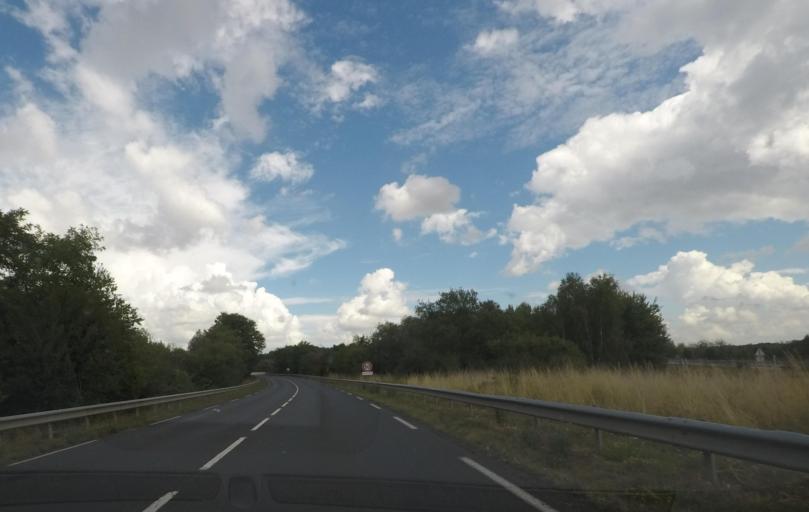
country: FR
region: Pays de la Loire
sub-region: Departement de la Sarthe
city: Champagne
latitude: 48.0482
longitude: 0.2934
